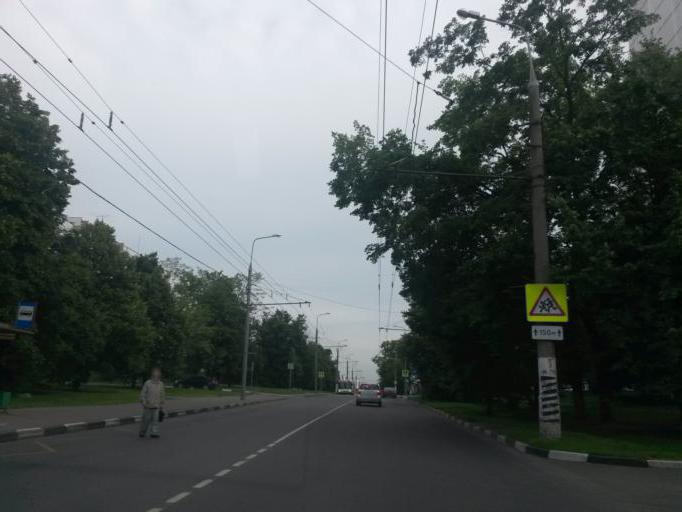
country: RU
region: Moscow
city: Orekhovo-Borisovo
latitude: 55.6180
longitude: 37.7436
